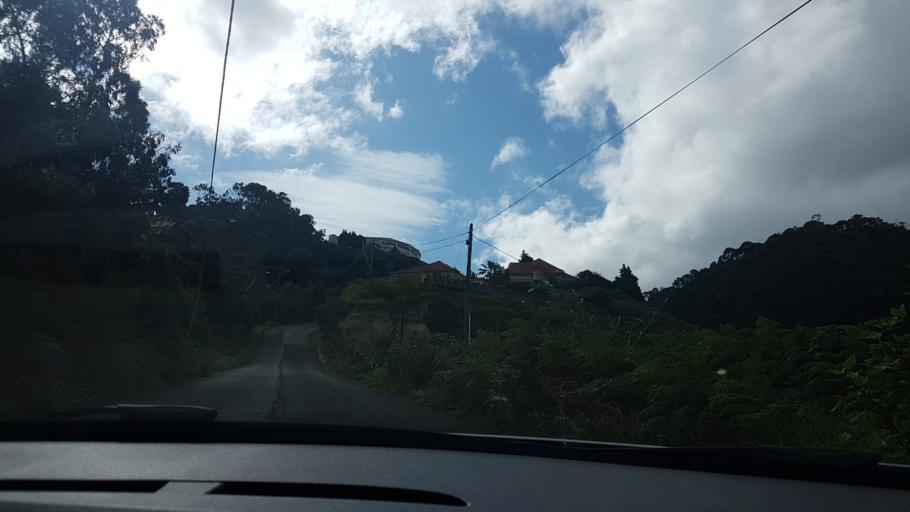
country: PT
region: Madeira
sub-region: Santa Cruz
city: Santa Cruz
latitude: 32.7312
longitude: -16.8228
